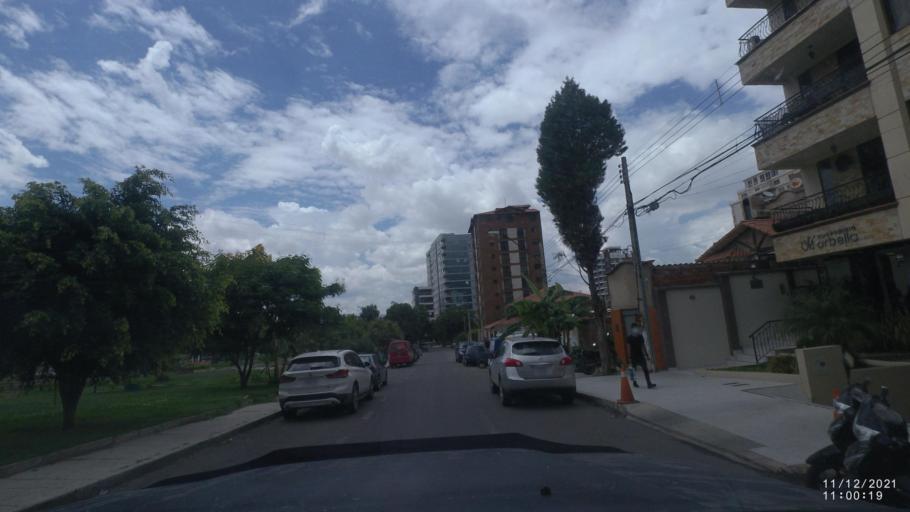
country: BO
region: Cochabamba
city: Cochabamba
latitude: -17.3722
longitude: -66.1449
